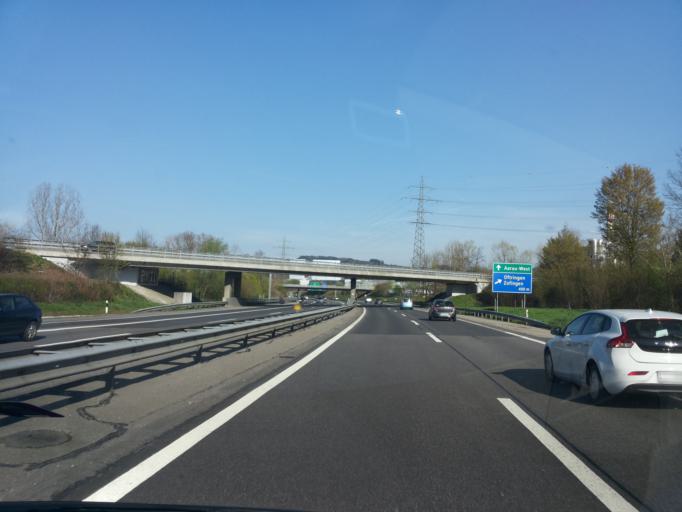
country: CH
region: Aargau
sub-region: Bezirk Zofingen
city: Oftringen
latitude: 47.3042
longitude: 7.9181
